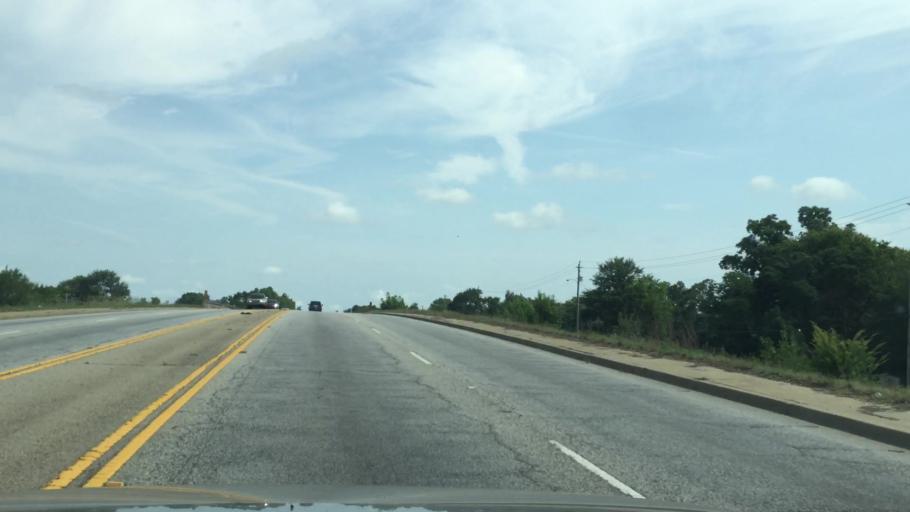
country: US
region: South Carolina
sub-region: Sumter County
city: South Sumter
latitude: 33.9049
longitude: -80.3538
